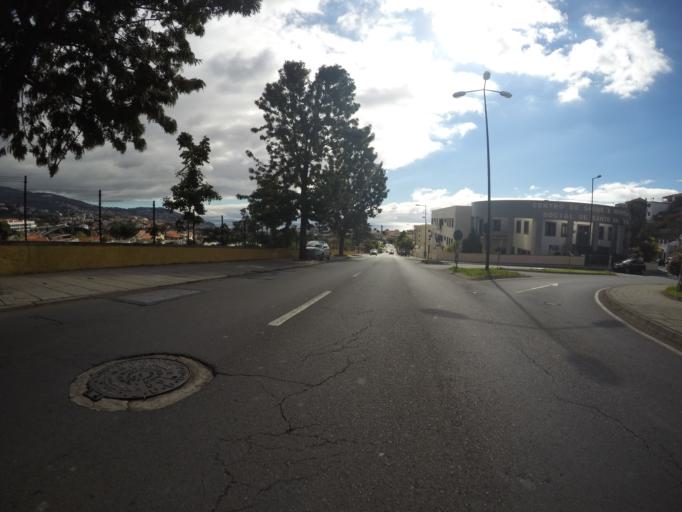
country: PT
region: Madeira
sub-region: Funchal
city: Nossa Senhora do Monte
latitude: 32.6646
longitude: -16.9361
